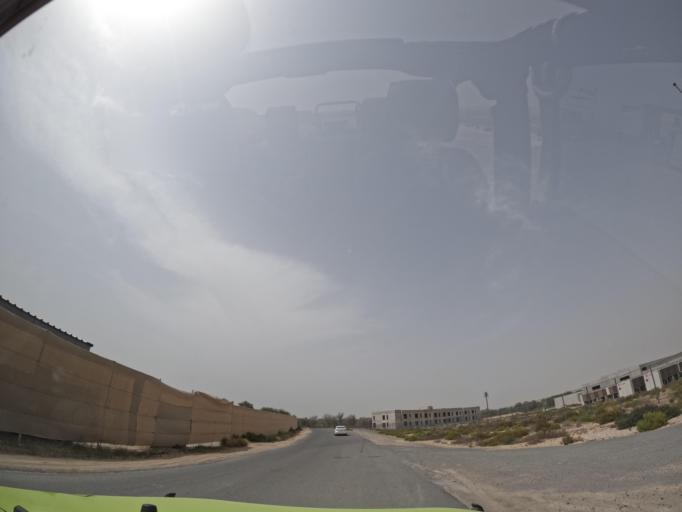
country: AE
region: Dubai
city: Dubai
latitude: 25.1314
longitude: 55.3357
